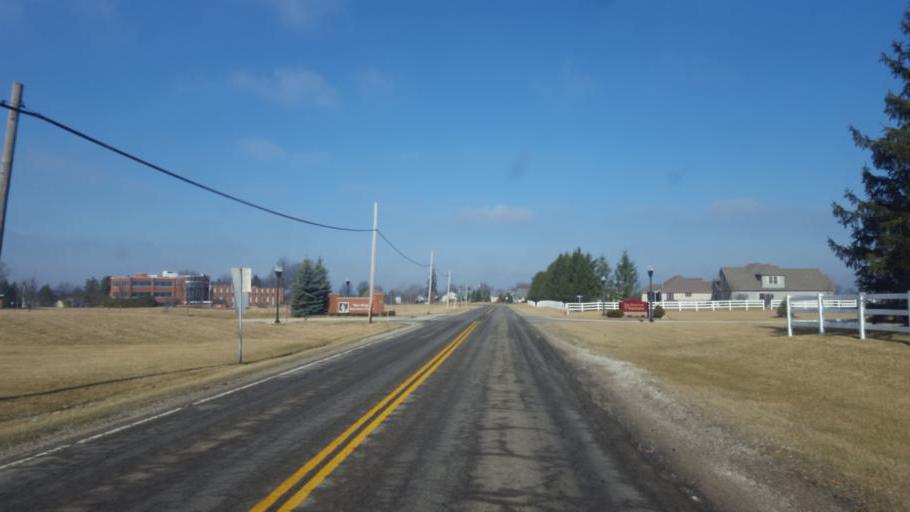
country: US
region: Ohio
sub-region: Crawford County
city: Bucyrus
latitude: 40.7912
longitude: -82.9491
